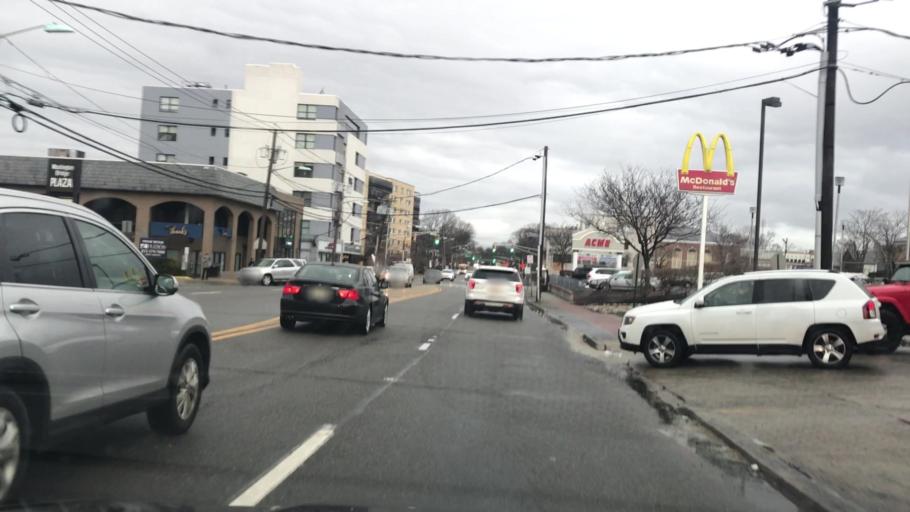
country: US
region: New Jersey
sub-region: Bergen County
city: Fort Lee
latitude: 40.8556
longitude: -73.9672
